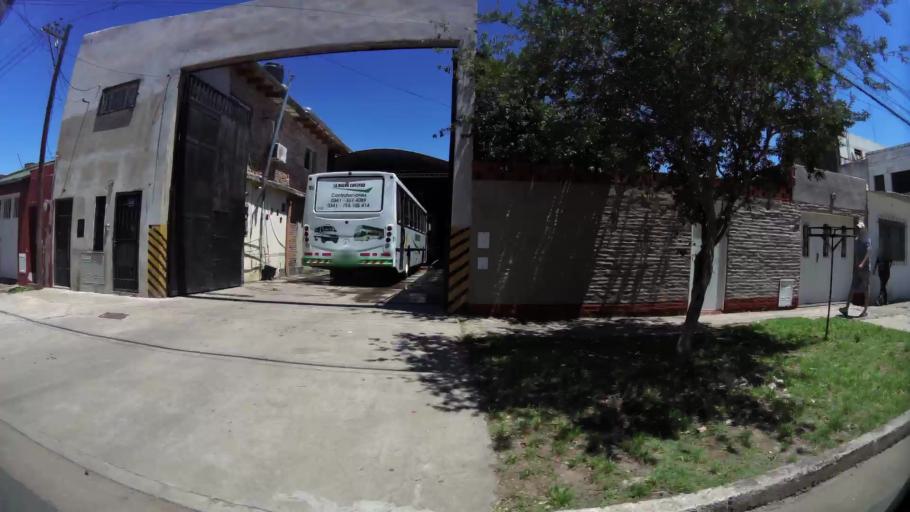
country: AR
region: Santa Fe
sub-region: Departamento de Rosario
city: Rosario
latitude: -32.9528
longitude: -60.7098
